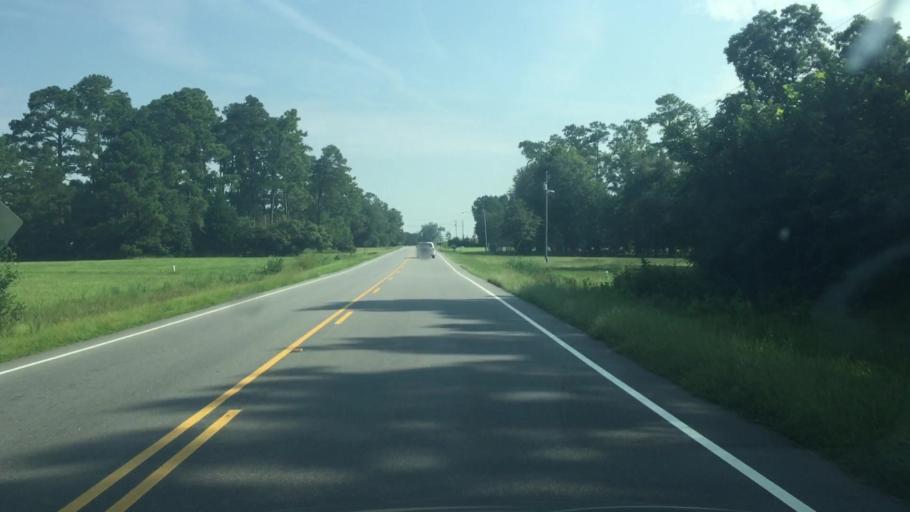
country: US
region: North Carolina
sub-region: Columbus County
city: Tabor City
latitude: 34.1626
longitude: -78.8460
